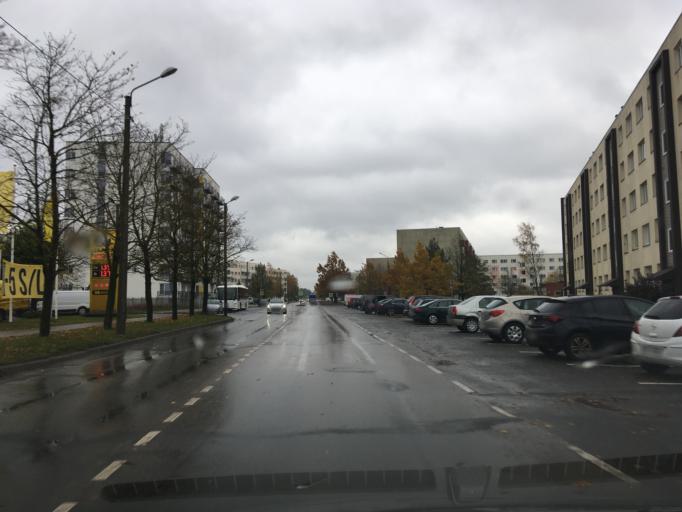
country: EE
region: Paernumaa
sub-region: Paernu linn
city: Parnu
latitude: 58.3710
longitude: 24.5370
